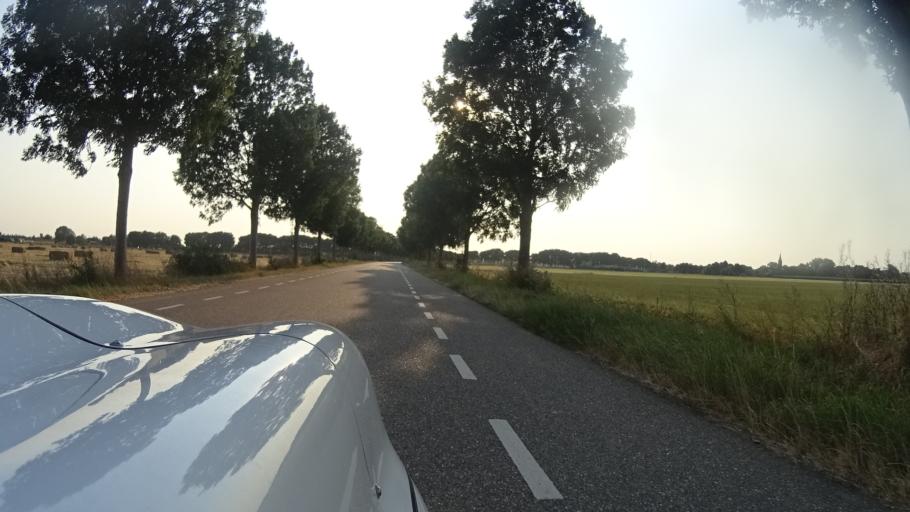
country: NL
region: Gelderland
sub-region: Gemeente Druten
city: Druten
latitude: 51.8427
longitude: 5.5736
